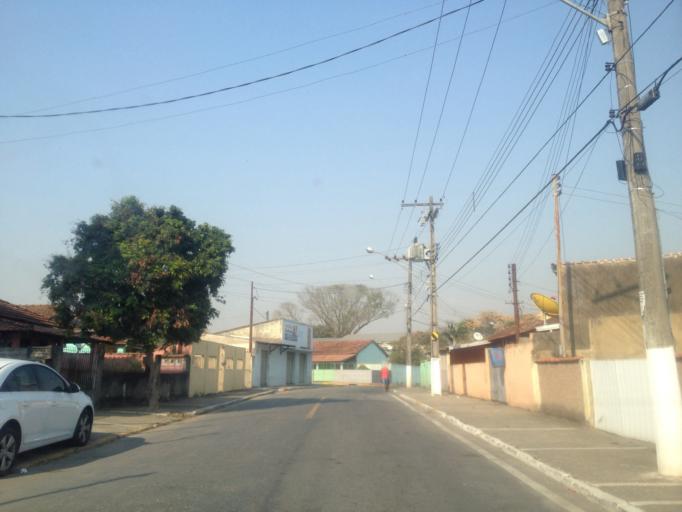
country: BR
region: Rio de Janeiro
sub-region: Porto Real
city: Porto Real
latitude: -22.4637
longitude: -44.3551
